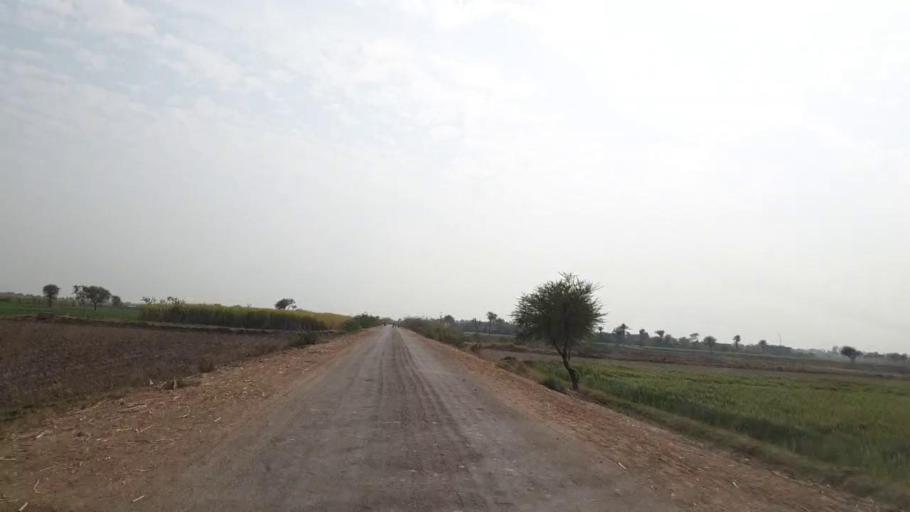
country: PK
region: Sindh
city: Mirpur Khas
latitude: 25.5329
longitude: 69.1567
